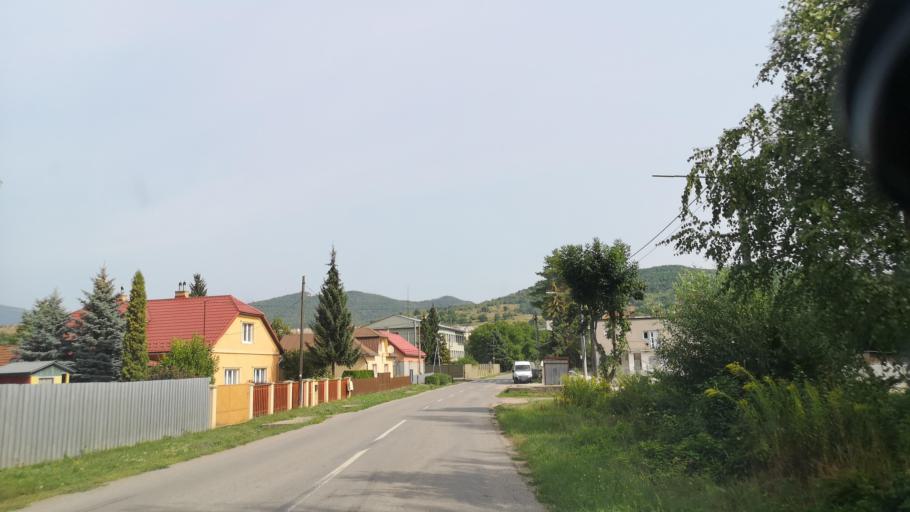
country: SK
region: Banskobystricky
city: Revuca
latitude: 48.6244
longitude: 20.2390
